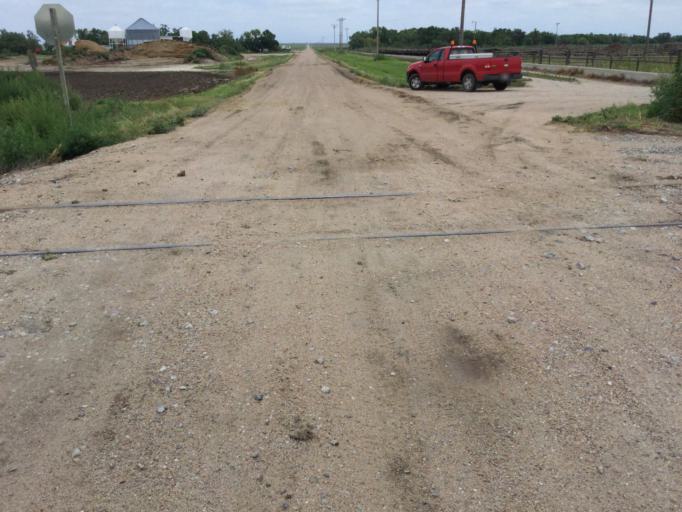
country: US
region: Kansas
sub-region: Rush County
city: La Crosse
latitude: 38.4696
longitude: -99.5116
